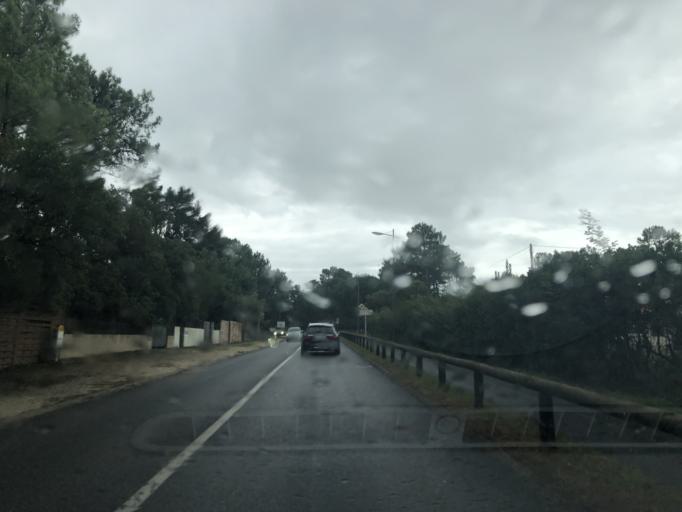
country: FR
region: Aquitaine
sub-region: Departement de la Gironde
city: Arcachon
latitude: 44.6904
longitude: -1.2396
